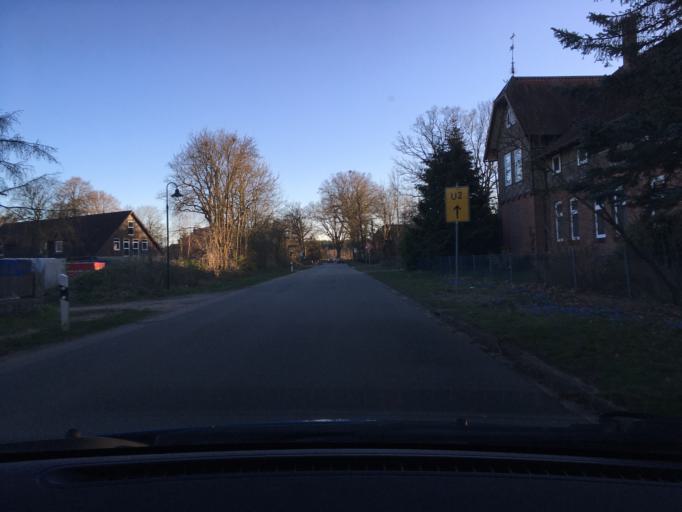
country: DE
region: Lower Saxony
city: Bleckede
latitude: 53.2629
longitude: 10.7432
